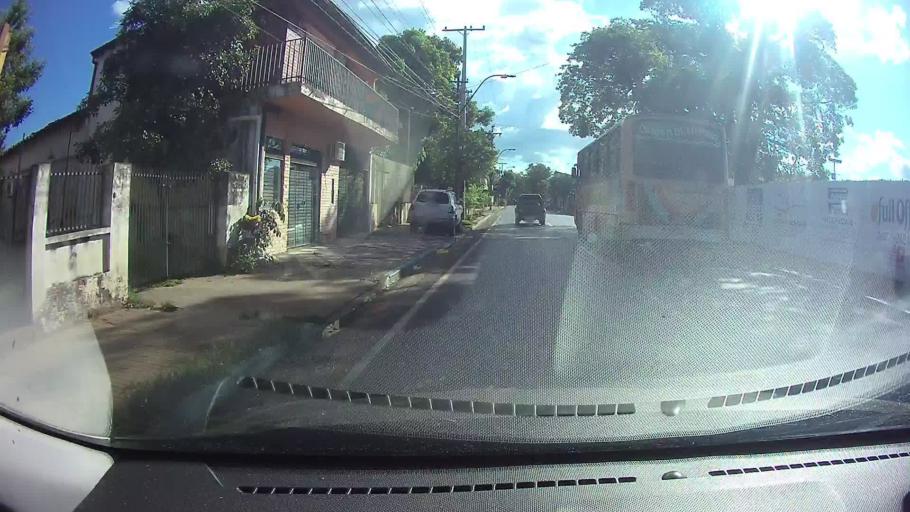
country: PY
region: Cordillera
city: Caacupe
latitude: -25.3827
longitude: -57.1375
